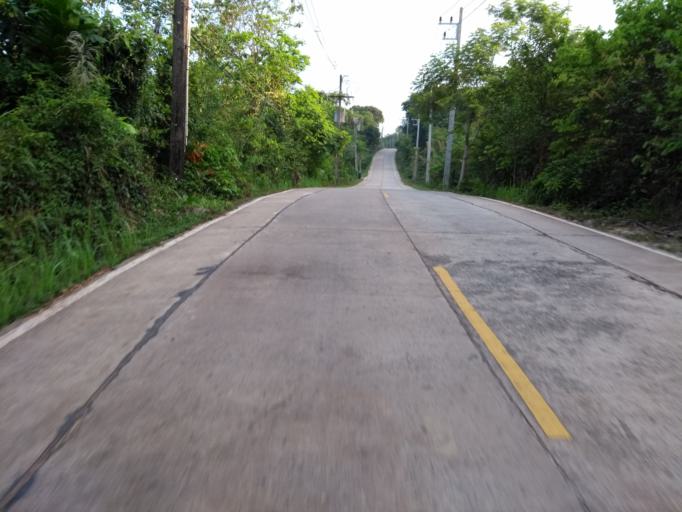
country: TH
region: Trat
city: Ko Kut
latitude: 11.6261
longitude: 102.5468
